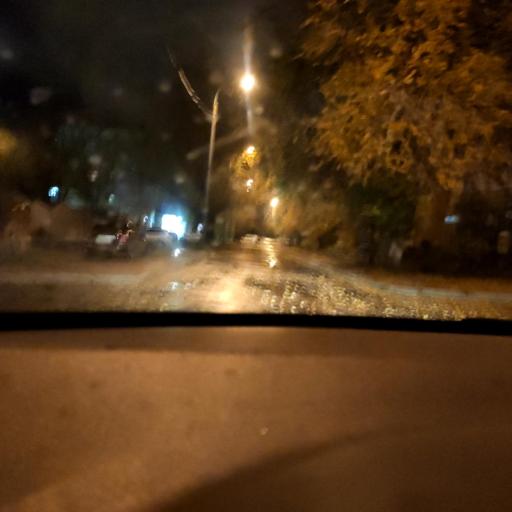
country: RU
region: Samara
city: Samara
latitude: 53.2065
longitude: 50.1838
